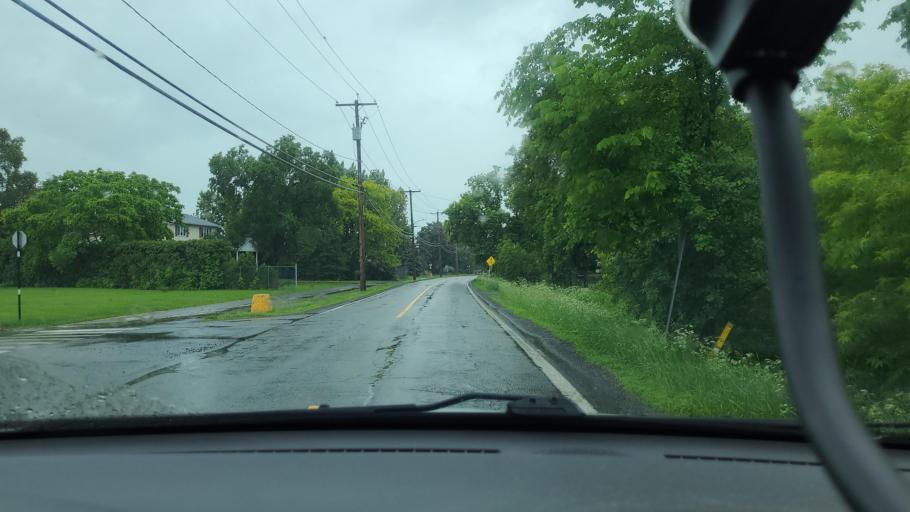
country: CA
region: Quebec
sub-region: Monteregie
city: Saint-Basile-le-Grand
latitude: 45.5377
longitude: -73.2777
